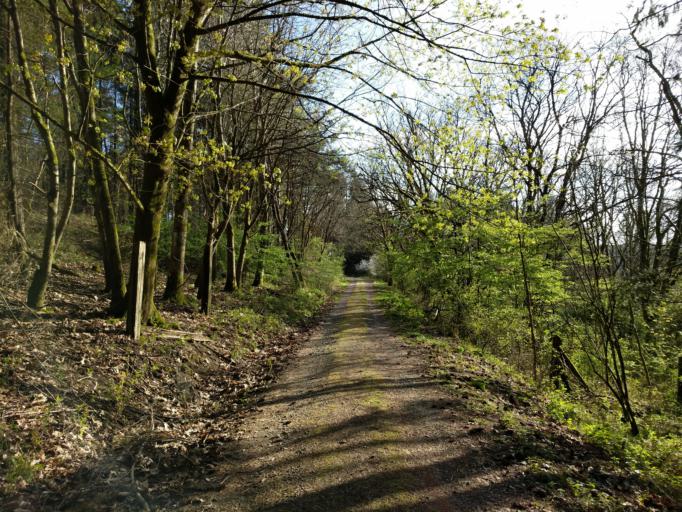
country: DE
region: Hesse
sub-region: Regierungsbezirk Giessen
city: Bad Endbach
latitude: 50.7603
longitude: 8.4853
